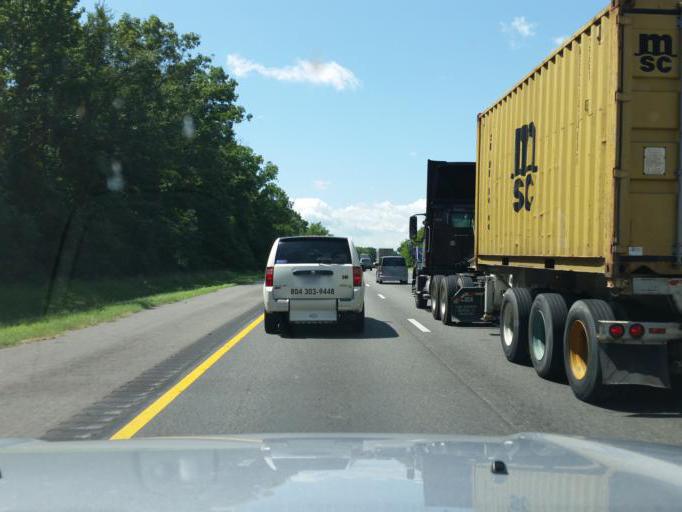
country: US
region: Virginia
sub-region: Hanover County
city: Ashland
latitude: 37.7879
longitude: -77.4600
